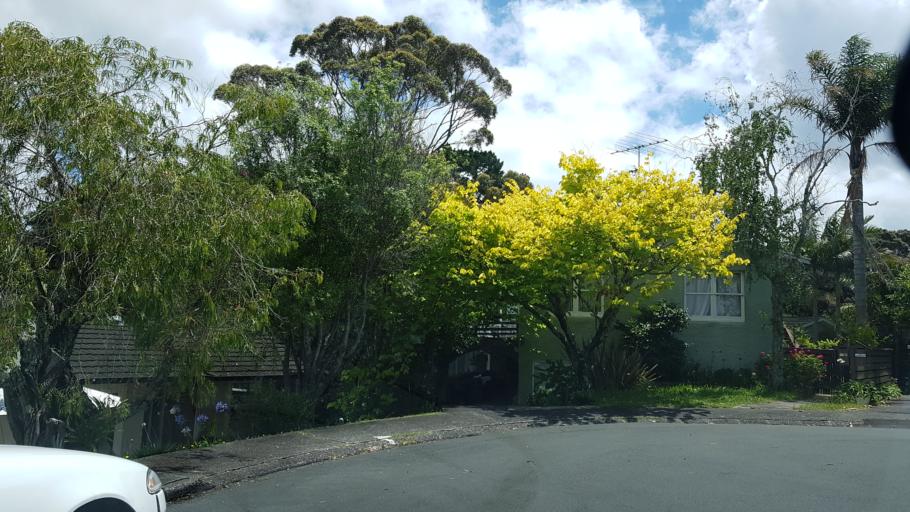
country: NZ
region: Auckland
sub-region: Auckland
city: North Shore
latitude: -36.8045
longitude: 174.7419
